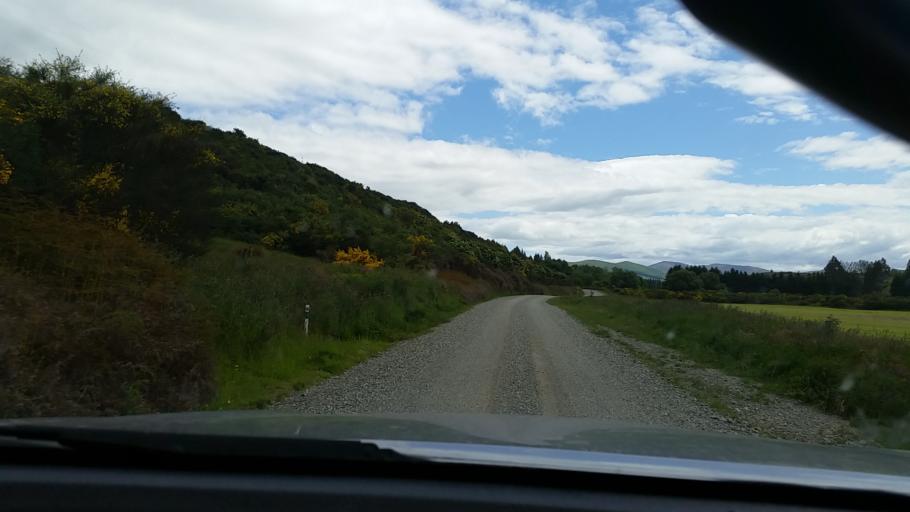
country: NZ
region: Otago
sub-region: Queenstown-Lakes District
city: Kingston
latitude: -45.7503
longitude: 168.5888
